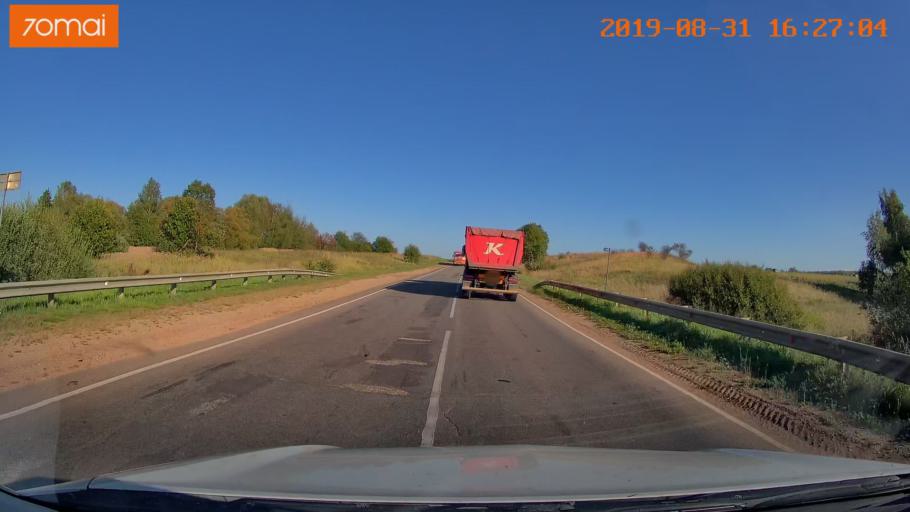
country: RU
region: Kaluga
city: Babynino
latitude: 54.5153
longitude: 35.7503
